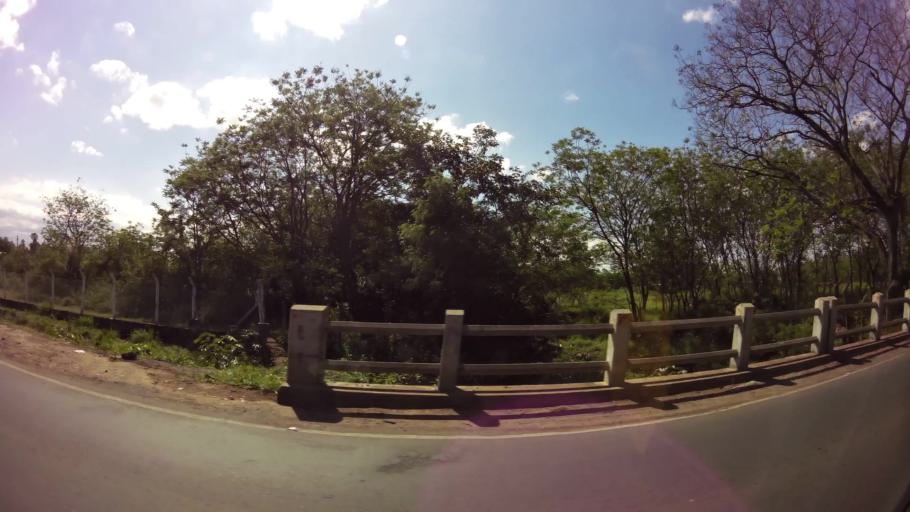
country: PY
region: Central
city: Fernando de la Mora
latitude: -25.2656
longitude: -57.5219
